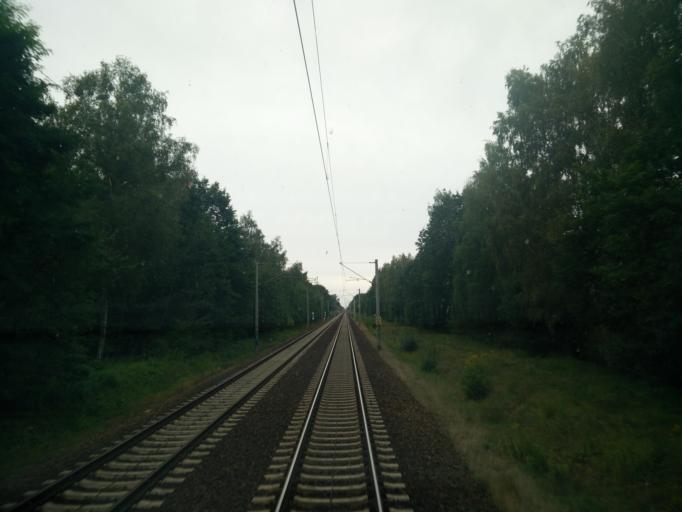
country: DE
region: Brandenburg
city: Dallgow-Doeberitz
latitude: 52.5675
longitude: 13.0598
